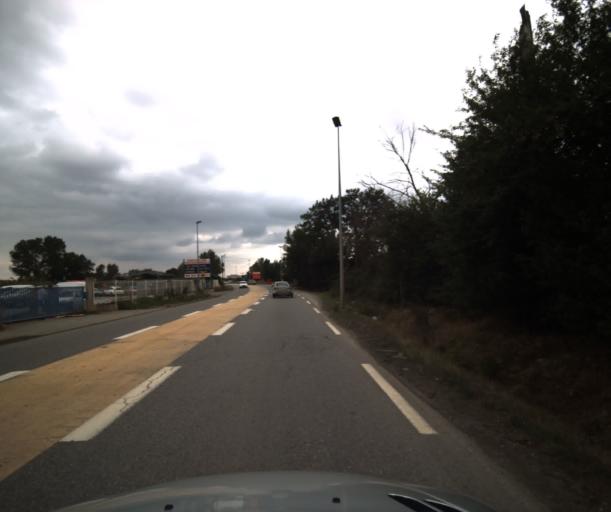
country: FR
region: Midi-Pyrenees
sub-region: Departement de la Haute-Garonne
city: Portet-sur-Garonne
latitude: 43.5347
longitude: 1.3877
